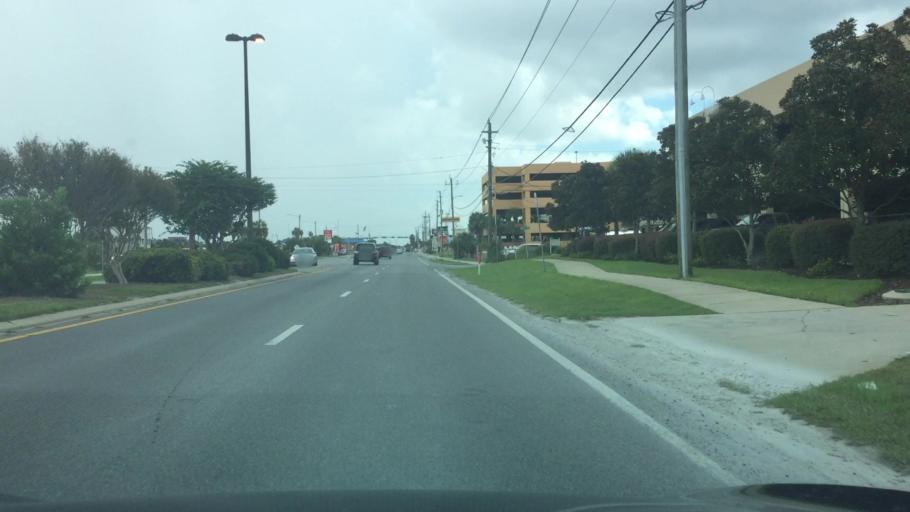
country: US
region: Florida
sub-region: Bay County
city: Lower Grand Lagoon
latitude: 30.1417
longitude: -85.7535
